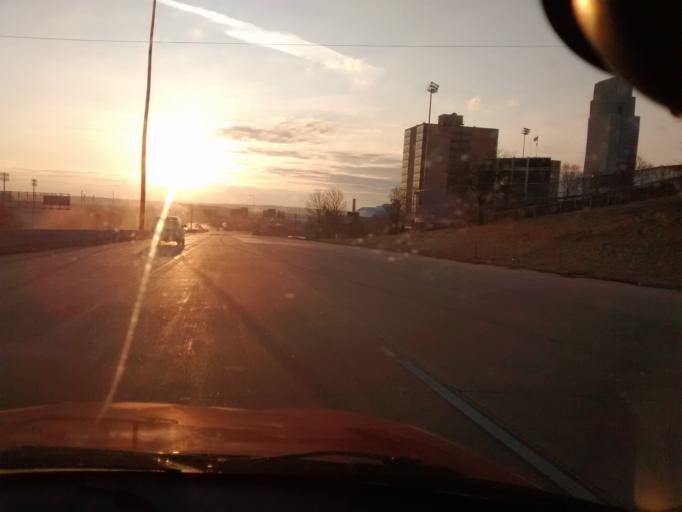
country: US
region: Nebraska
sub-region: Douglas County
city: Omaha
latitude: 41.2631
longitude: -95.9454
